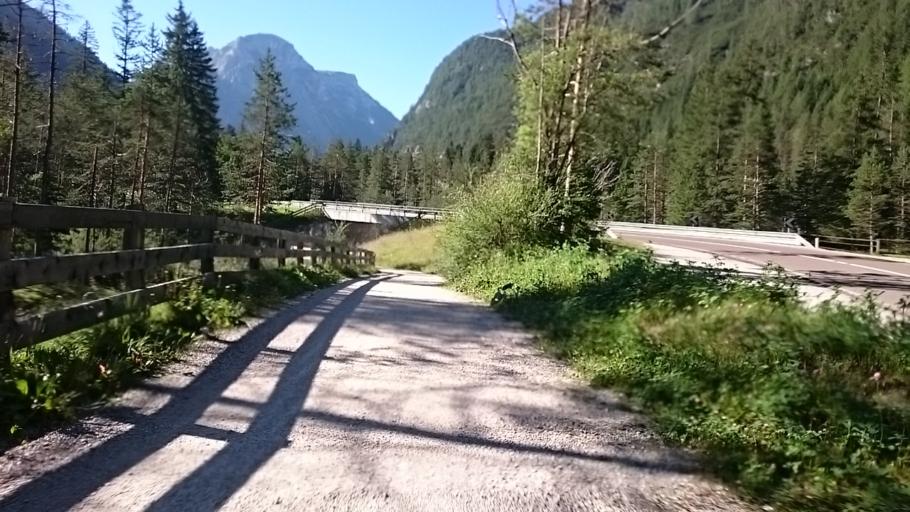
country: IT
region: Trentino-Alto Adige
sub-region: Bolzano
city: Dobbiaco
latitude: 46.6570
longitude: 12.2257
